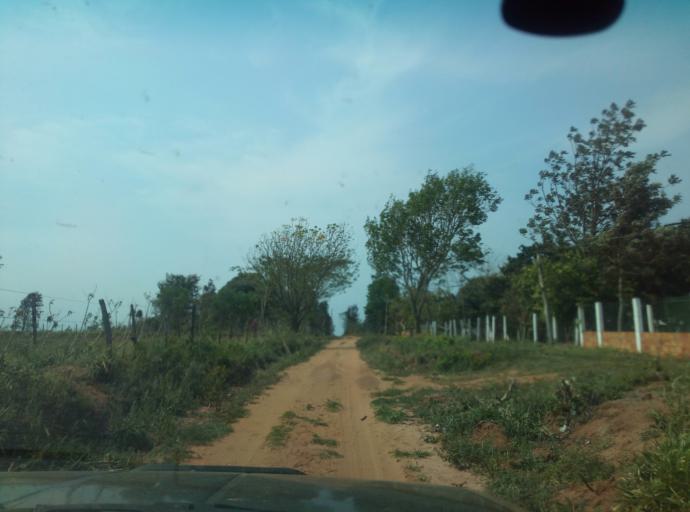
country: PY
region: Caaguazu
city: San Joaquin
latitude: -25.1453
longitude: -56.0992
